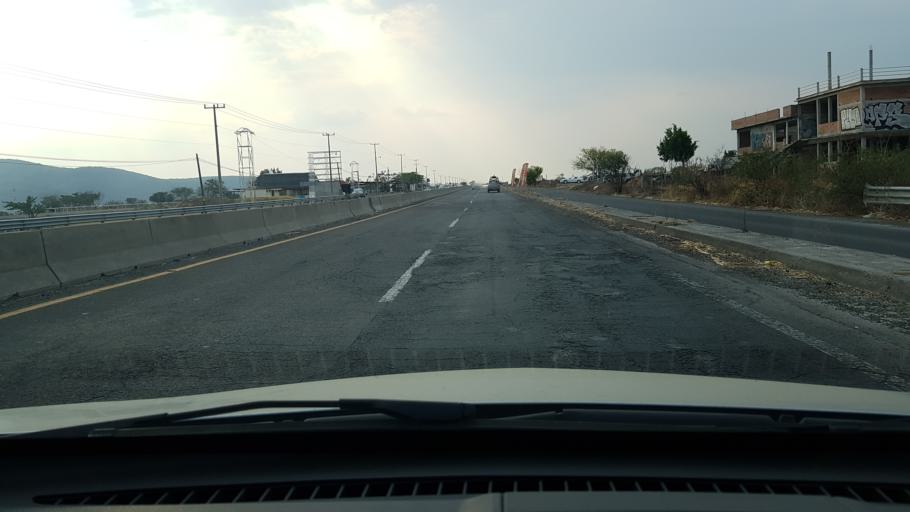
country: MX
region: Morelos
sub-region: Ayala
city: Unidad Habitacional Mariano Matamoros
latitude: 18.7390
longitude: -98.8279
